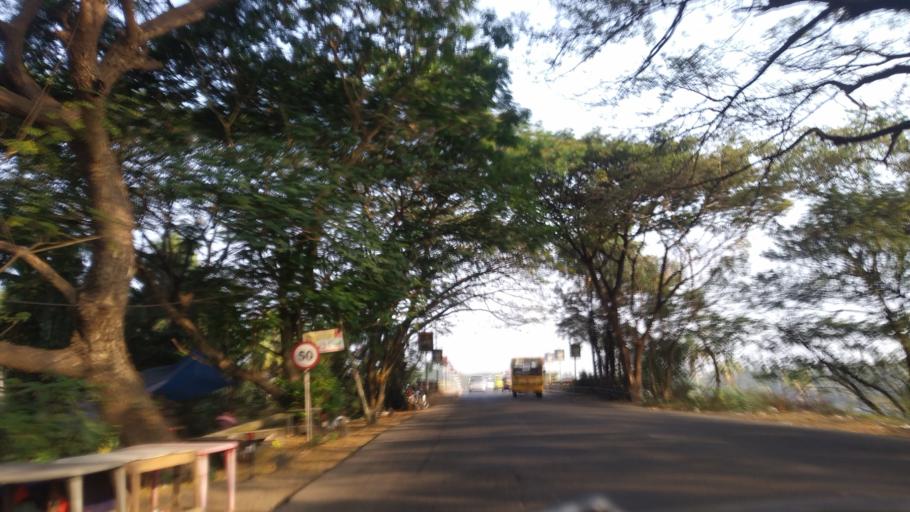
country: IN
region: Kerala
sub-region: Thrissur District
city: Kodungallur
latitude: 10.1976
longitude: 76.2007
